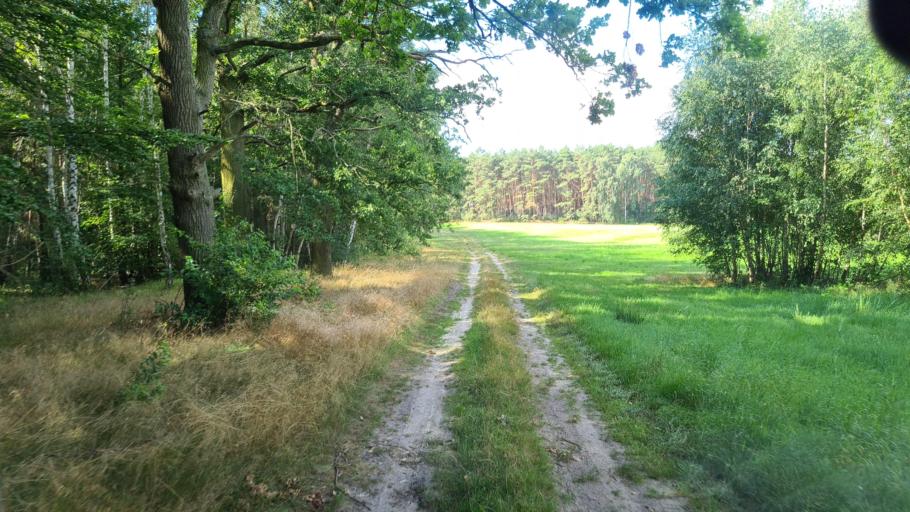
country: DE
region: Brandenburg
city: Crinitz
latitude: 51.7457
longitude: 13.6986
